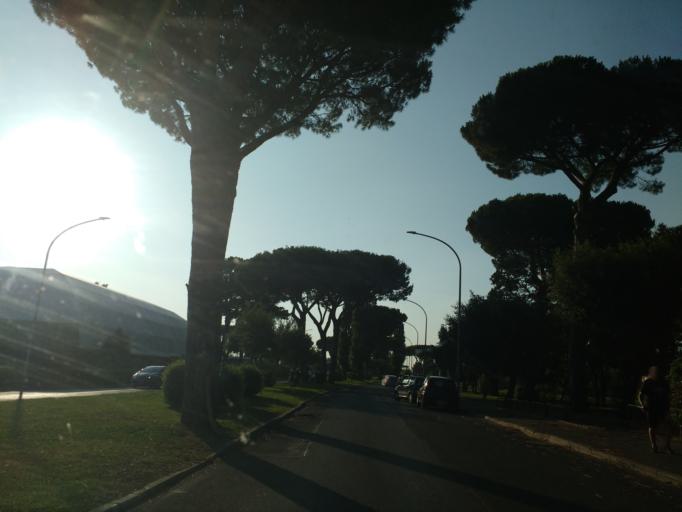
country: IT
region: Latium
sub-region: Citta metropolitana di Roma Capitale
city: Acilia-Castel Fusano-Ostia Antica
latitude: 41.7508
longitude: 12.3521
